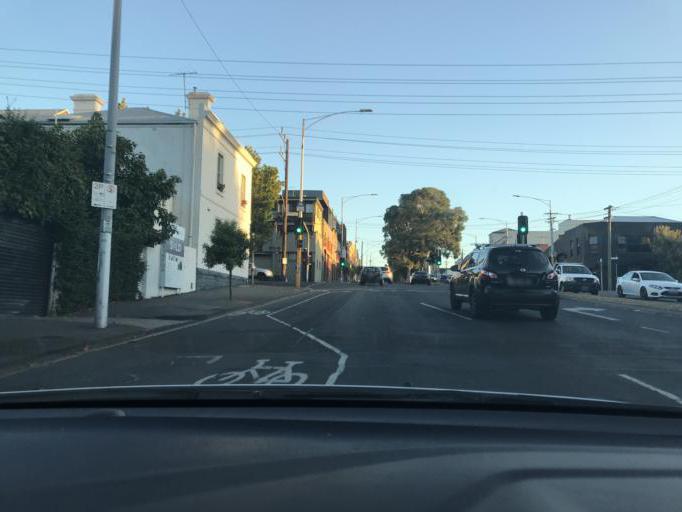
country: AU
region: Victoria
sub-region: Melbourne
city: North Melbourne
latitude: -37.8001
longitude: 144.9487
